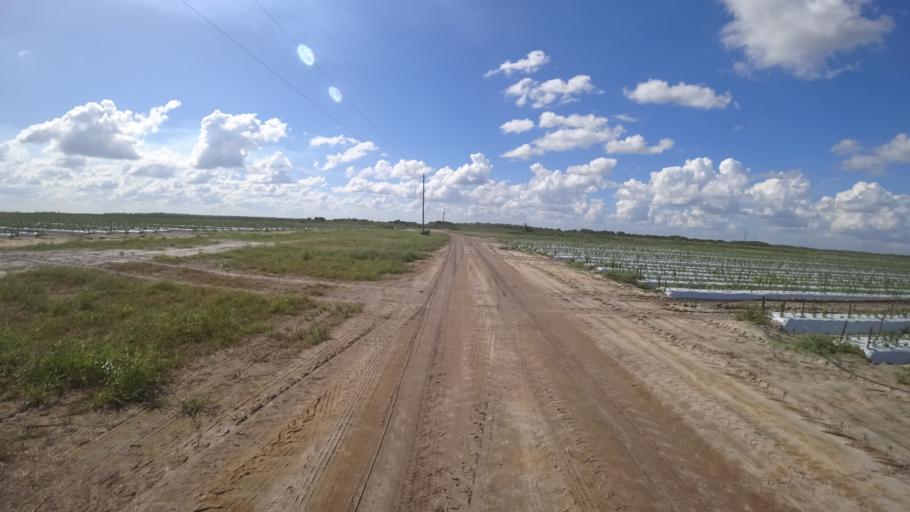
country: US
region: Florida
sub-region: DeSoto County
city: Arcadia
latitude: 27.3318
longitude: -82.0956
